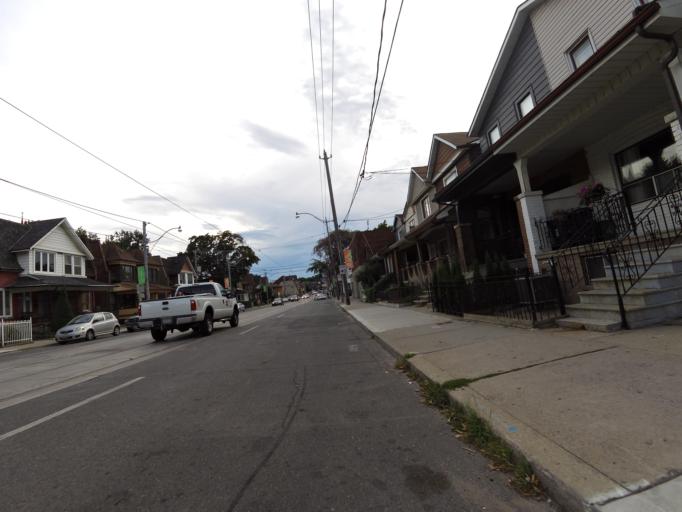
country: CA
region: Ontario
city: Toronto
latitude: 43.6518
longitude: -79.4368
